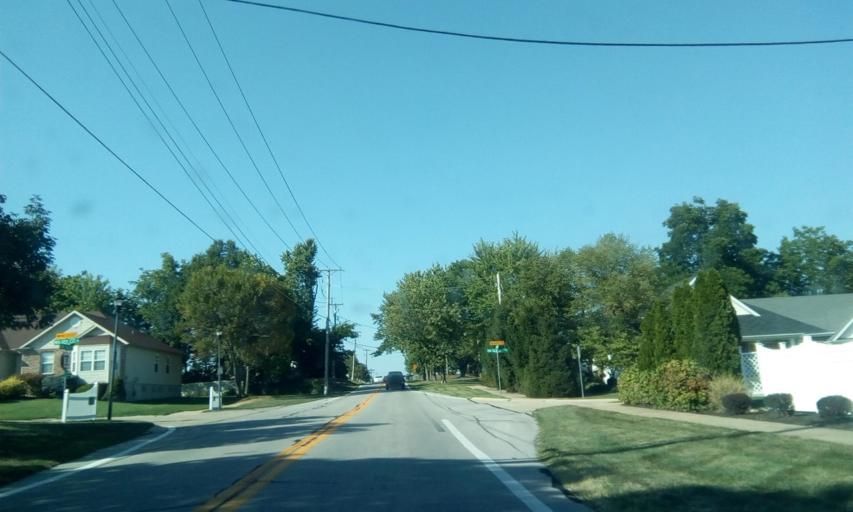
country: US
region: Missouri
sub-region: Saint Louis County
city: Green Park
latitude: 38.5115
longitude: -90.3428
